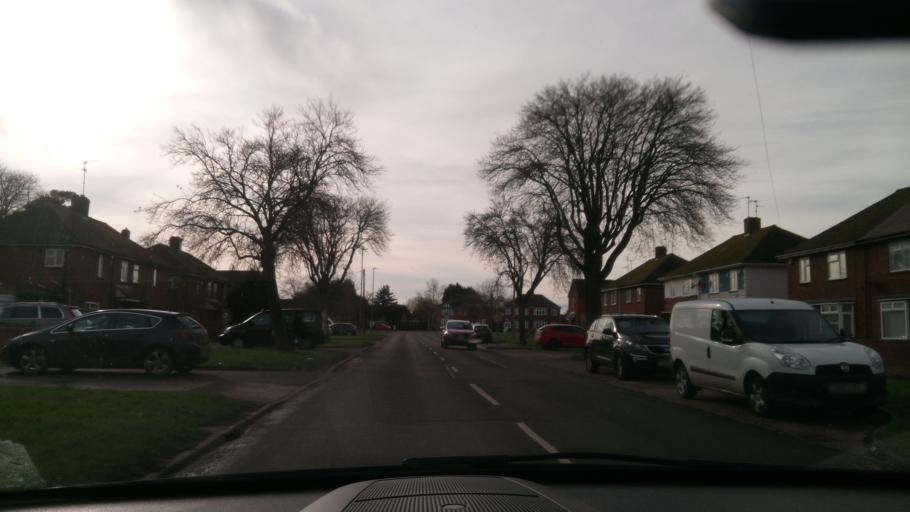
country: GB
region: England
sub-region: Peterborough
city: Peterborough
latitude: 52.5903
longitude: -0.2229
